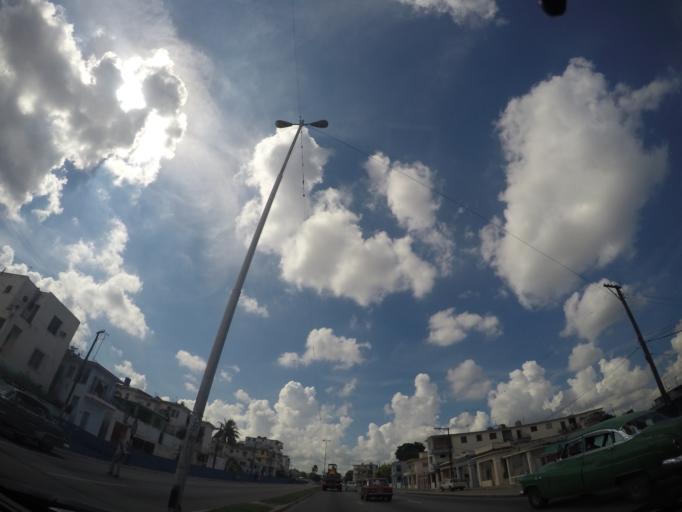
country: CU
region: La Habana
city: Cerro
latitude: 23.1035
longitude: -82.4199
